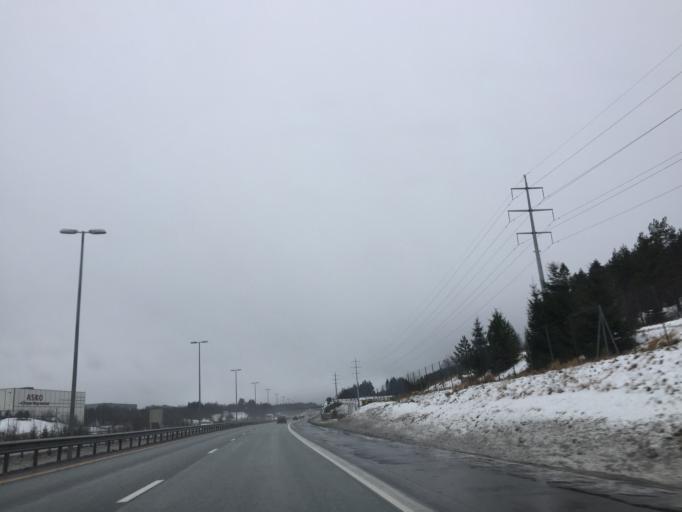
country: NO
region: Akershus
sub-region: Vestby
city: Vestby
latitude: 59.5920
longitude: 10.7381
